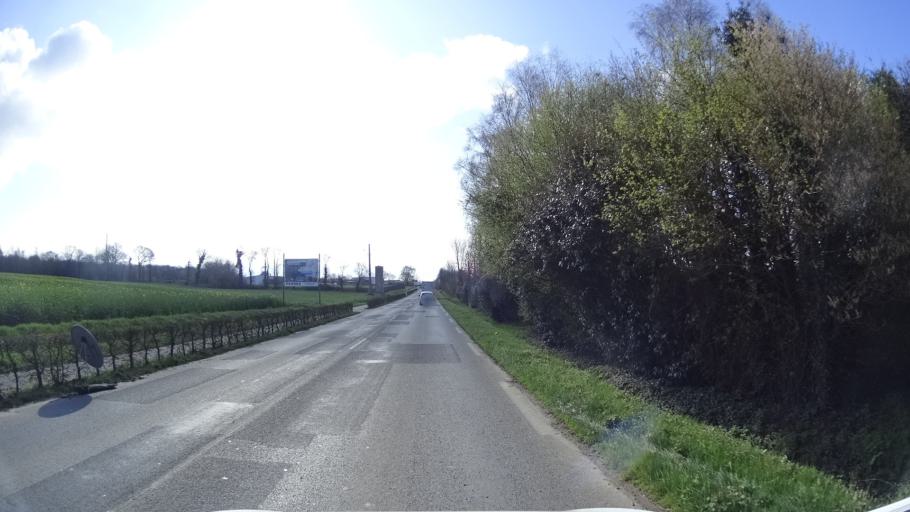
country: FR
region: Brittany
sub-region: Departement d'Ille-et-Vilaine
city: La Meziere
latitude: 48.2097
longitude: -1.7415
